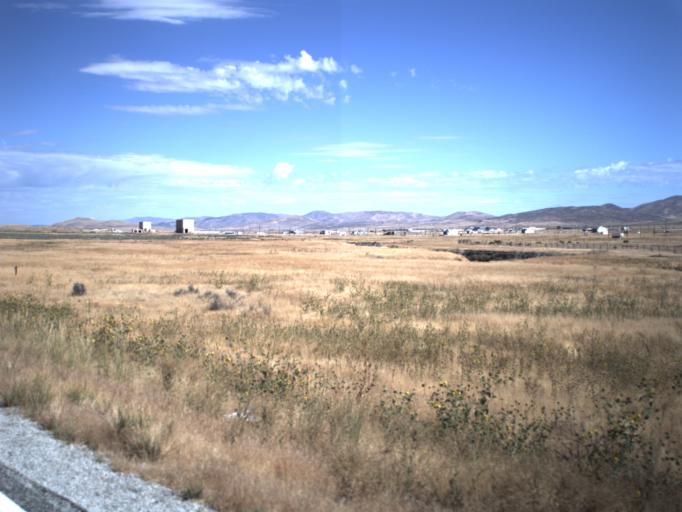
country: US
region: Utah
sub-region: Box Elder County
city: Tremonton
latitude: 41.6966
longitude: -112.4454
